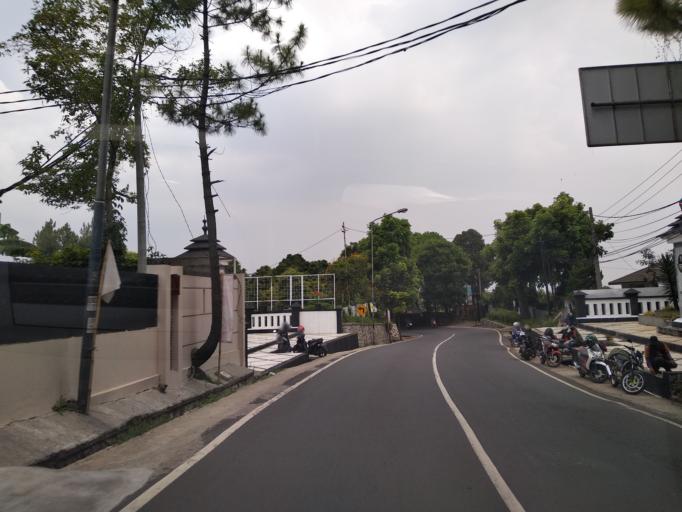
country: ID
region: West Java
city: Lembang
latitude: -6.8419
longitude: 107.5974
